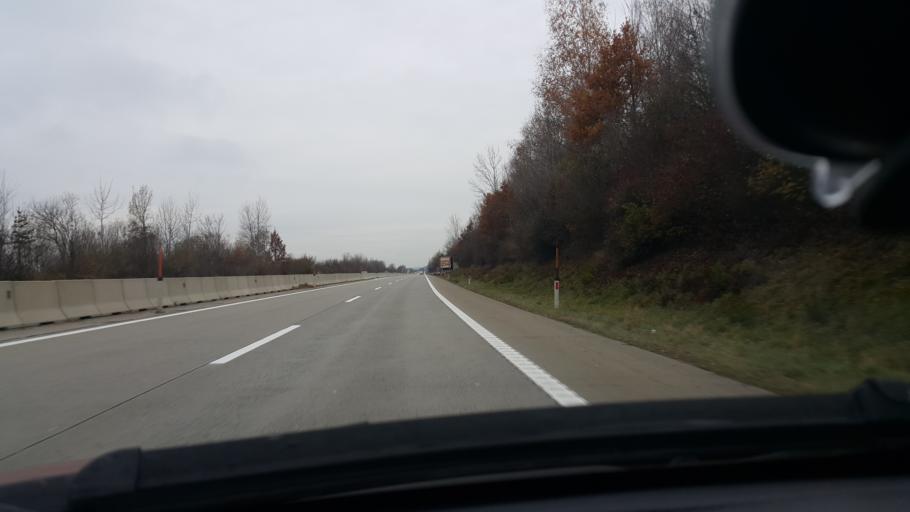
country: AT
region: Carinthia
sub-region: Politischer Bezirk Klagenfurt Land
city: Ebenthal
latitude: 46.6407
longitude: 14.3623
